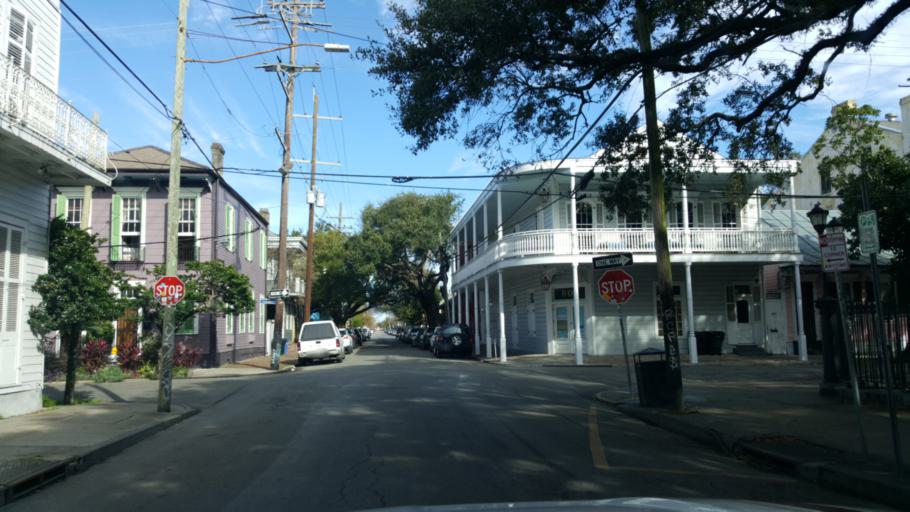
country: US
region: Louisiana
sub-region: Orleans Parish
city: New Orleans
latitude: 29.9653
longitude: -90.0579
